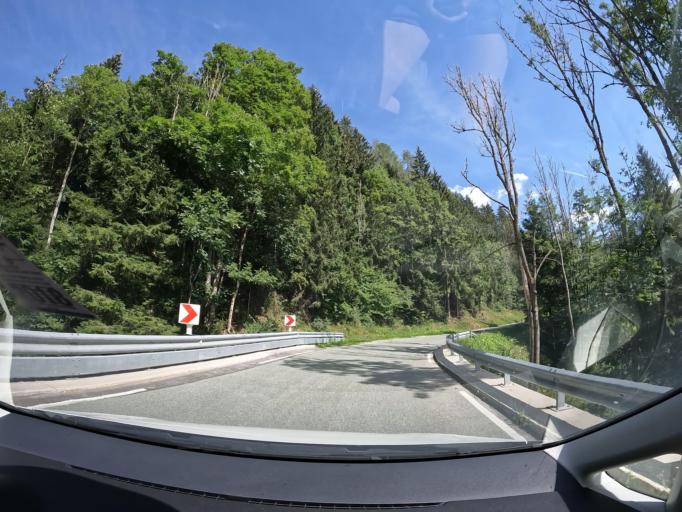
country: AT
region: Carinthia
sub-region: Politischer Bezirk Feldkirchen
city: Glanegg
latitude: 46.7385
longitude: 14.1974
